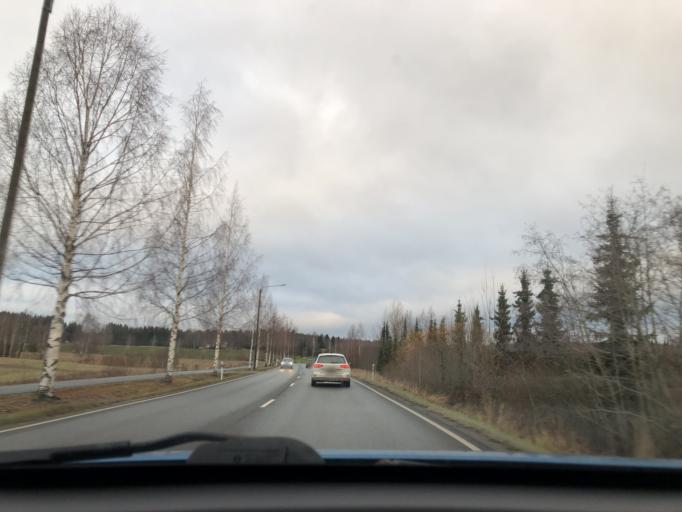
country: FI
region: Pirkanmaa
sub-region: Tampere
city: Kangasala
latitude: 61.4824
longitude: 24.0553
